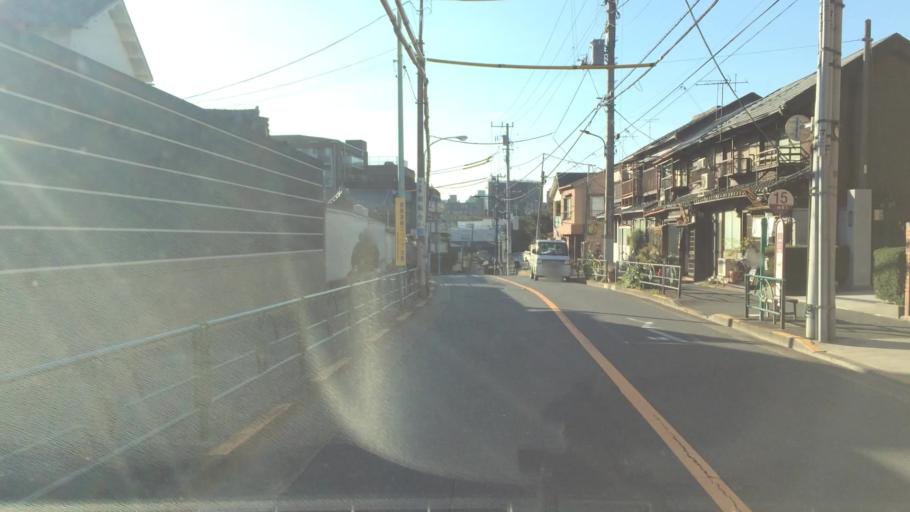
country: JP
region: Tokyo
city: Tokyo
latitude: 35.7237
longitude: 139.7679
